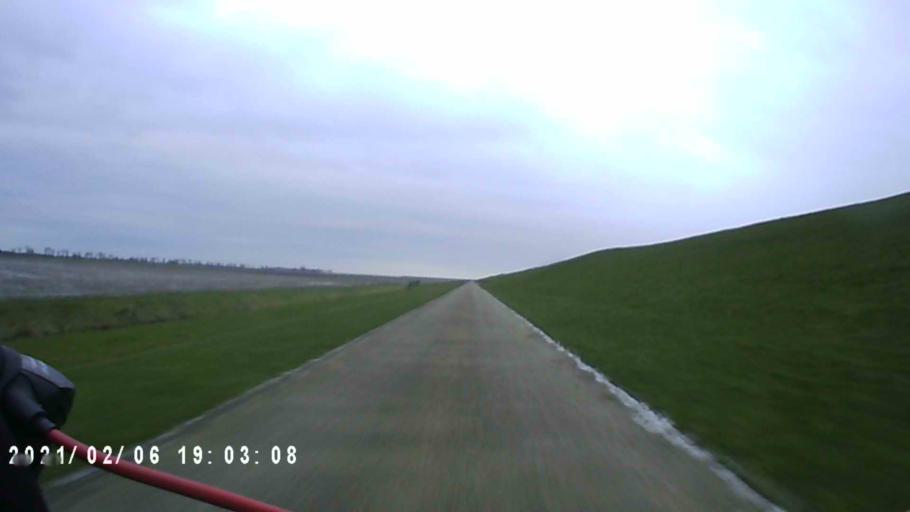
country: NL
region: Groningen
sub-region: Gemeente Winsum
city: Winsum
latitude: 53.4231
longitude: 6.4790
